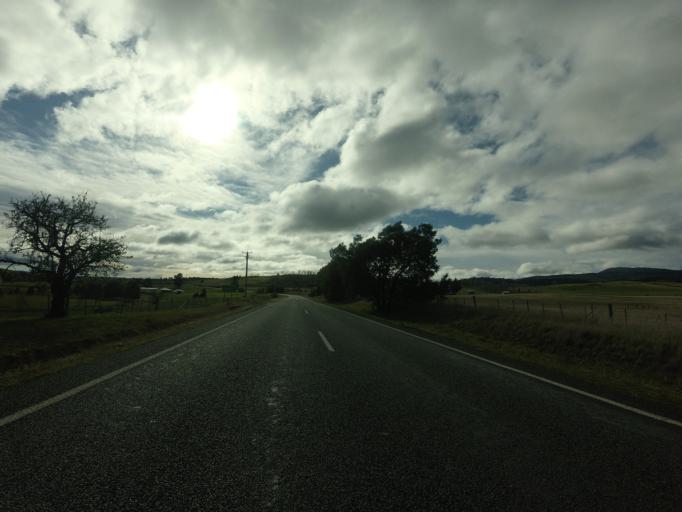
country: AU
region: Tasmania
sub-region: Derwent Valley
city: New Norfolk
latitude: -42.6627
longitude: 146.9337
